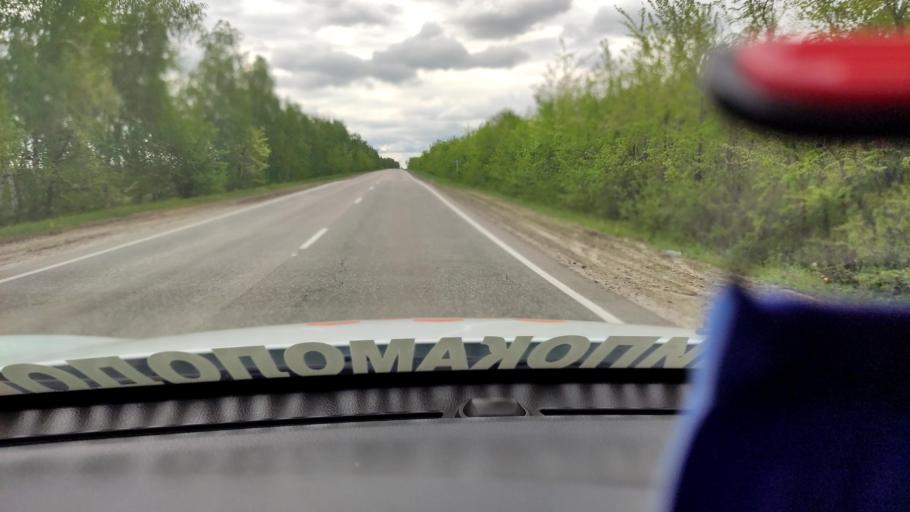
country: RU
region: Voronezj
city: Imeni Pervogo Maya
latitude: 50.7892
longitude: 39.3752
